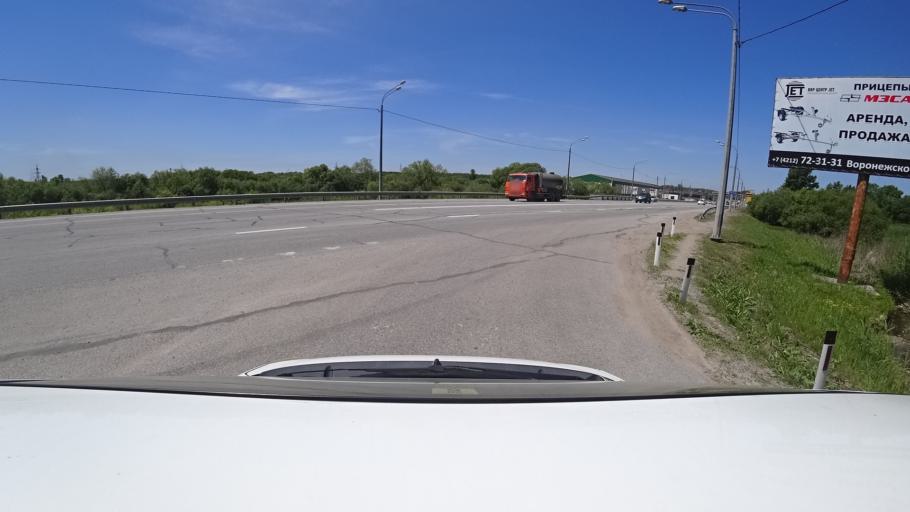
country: RU
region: Khabarovsk Krai
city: Topolevo
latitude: 48.5049
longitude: 135.1683
